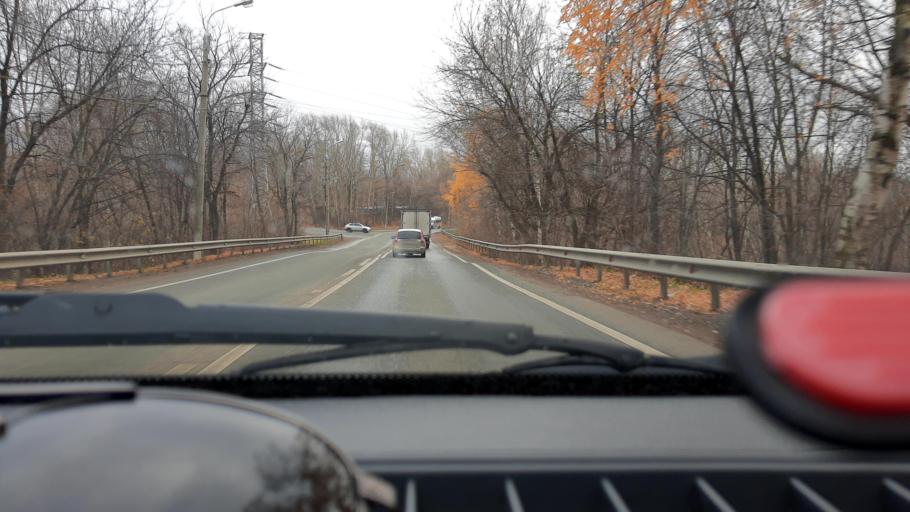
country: RU
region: Bashkortostan
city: Ufa
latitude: 54.8516
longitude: 56.0755
